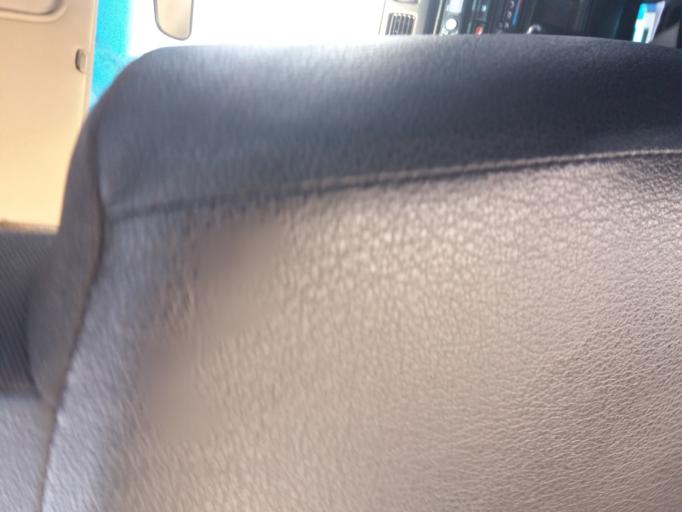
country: MX
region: Aguascalientes
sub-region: Aguascalientes
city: San Sebastian [Fraccionamiento]
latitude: 21.8063
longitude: -102.2905
